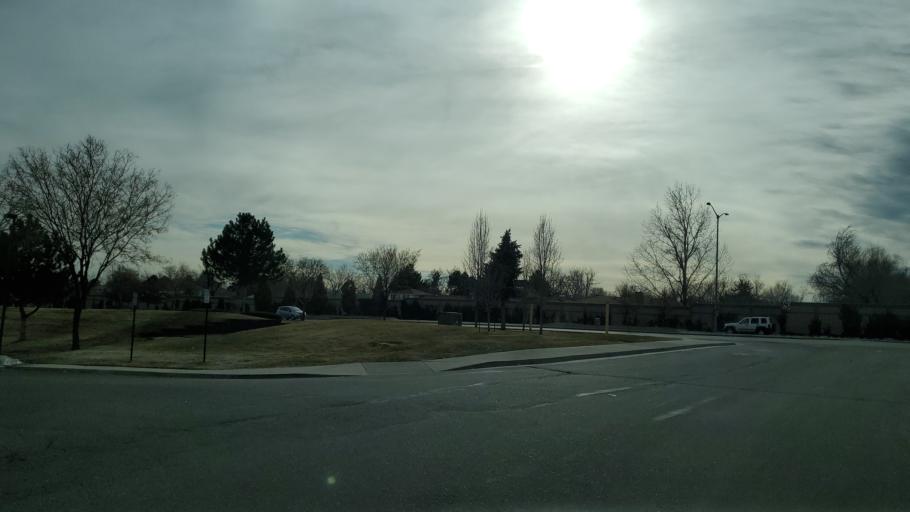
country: US
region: Colorado
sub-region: Adams County
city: Northglenn
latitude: 39.9144
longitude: -104.9498
